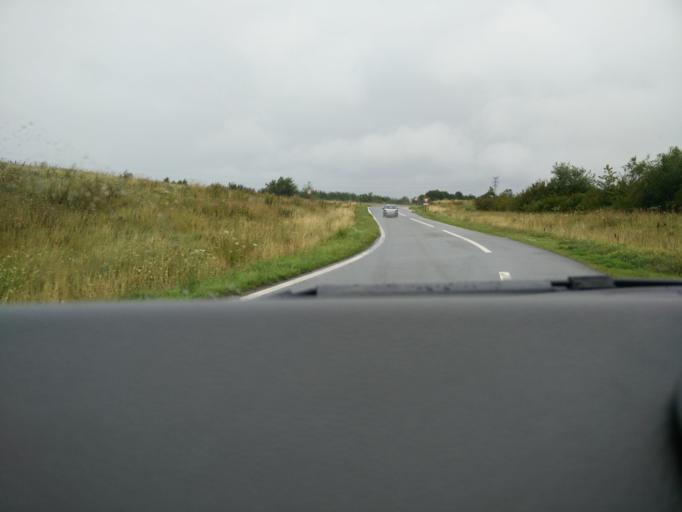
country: FR
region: Nord-Pas-de-Calais
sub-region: Departement du Pas-de-Calais
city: Marconnelle
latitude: 50.3689
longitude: 1.9417
